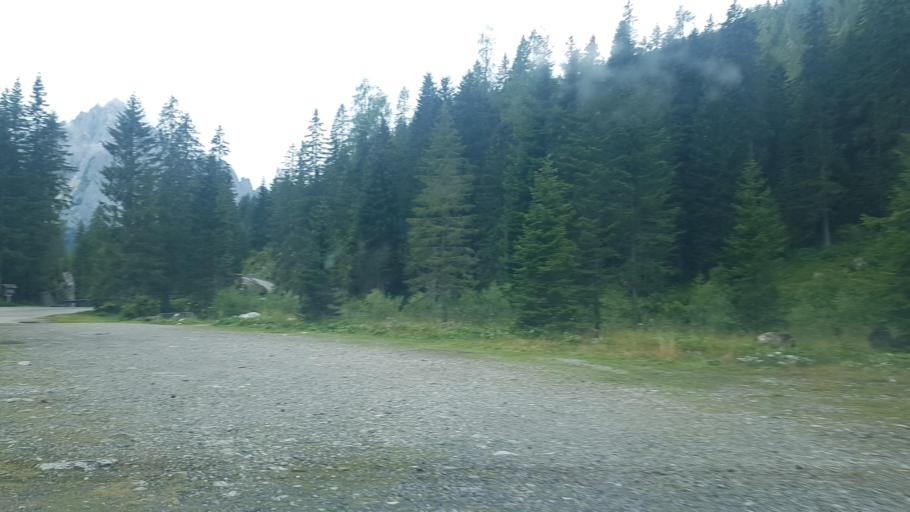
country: IT
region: Veneto
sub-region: Provincia di Belluno
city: Granvilla
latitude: 46.5861
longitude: 12.7272
